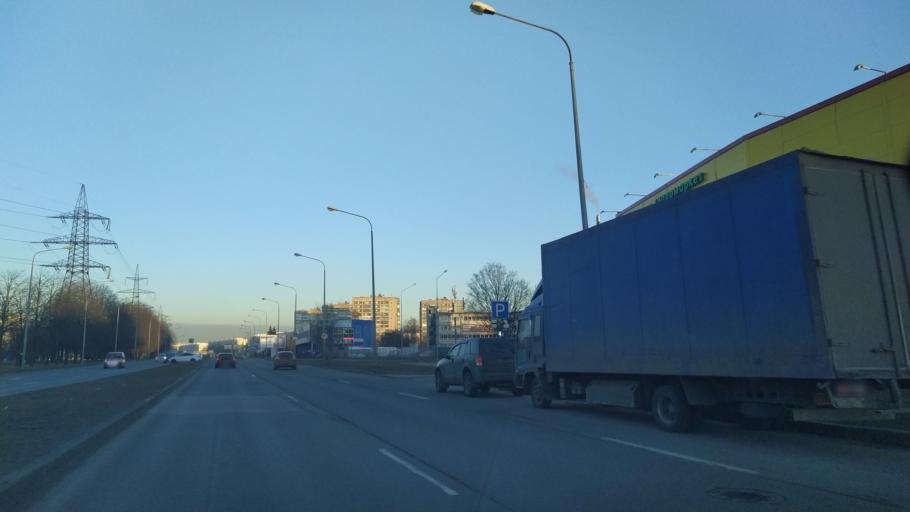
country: RU
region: Leningrad
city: Kalininskiy
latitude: 59.9759
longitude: 30.4079
